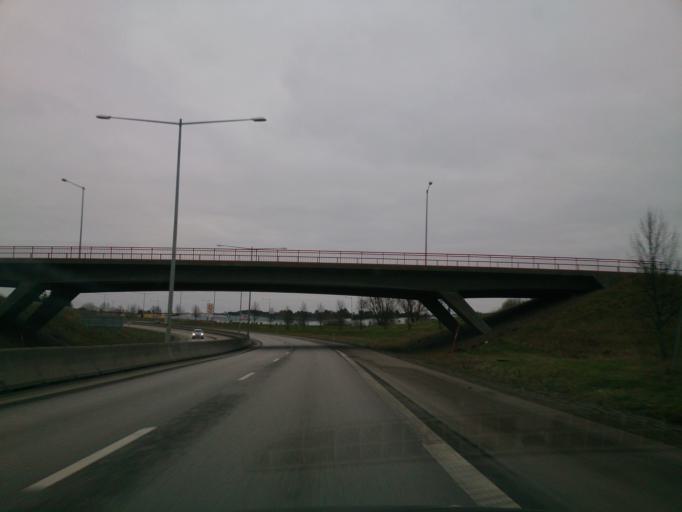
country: SE
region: OEstergoetland
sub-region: Norrkopings Kommun
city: Norrkoping
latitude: 58.5793
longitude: 16.1164
